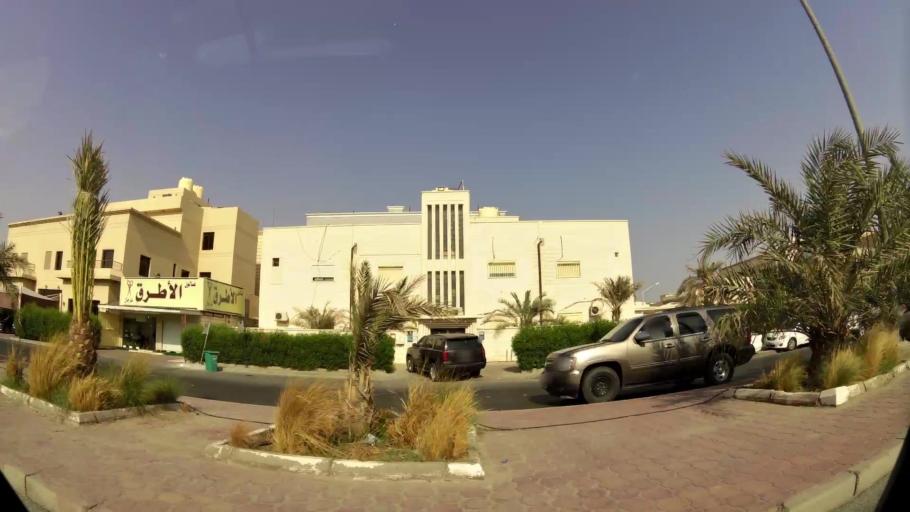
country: KW
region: Muhafazat al Jahra'
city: Al Jahra'
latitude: 29.3523
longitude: 47.6795
